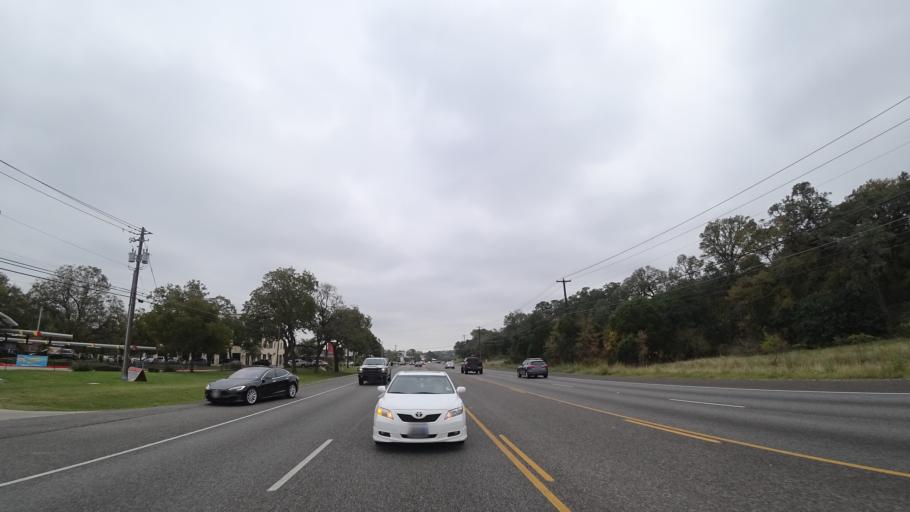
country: US
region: Texas
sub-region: Travis County
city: Barton Creek
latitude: 30.2428
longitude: -97.8829
